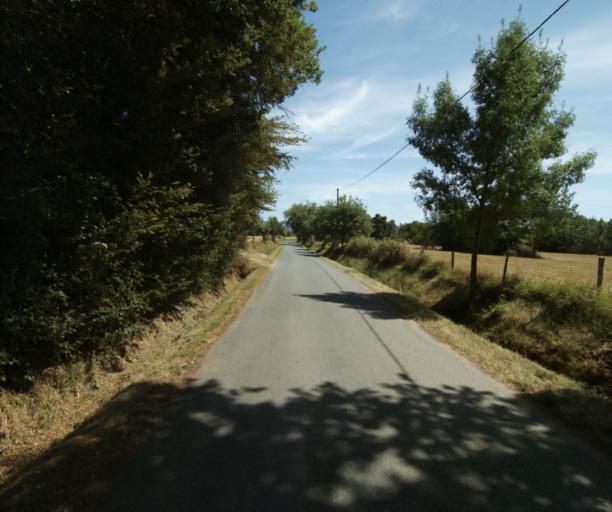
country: FR
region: Midi-Pyrenees
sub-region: Departement de la Haute-Garonne
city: Revel
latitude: 43.5017
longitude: 2.0012
